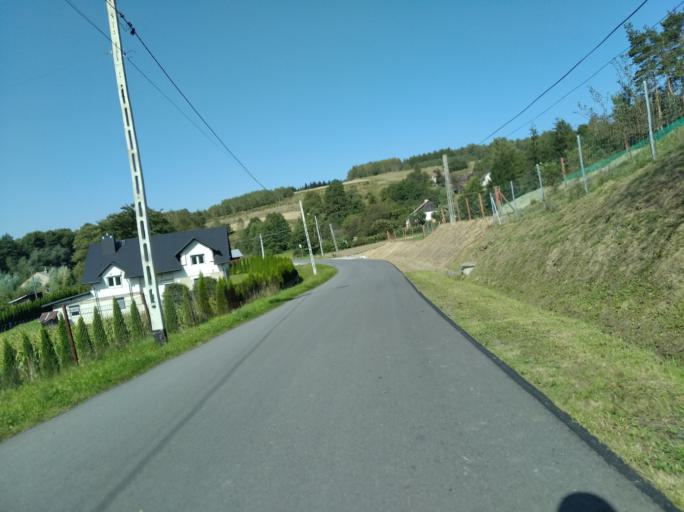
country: PL
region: Subcarpathian Voivodeship
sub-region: Powiat strzyzowski
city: Czudec
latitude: 49.9551
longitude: 21.8158
